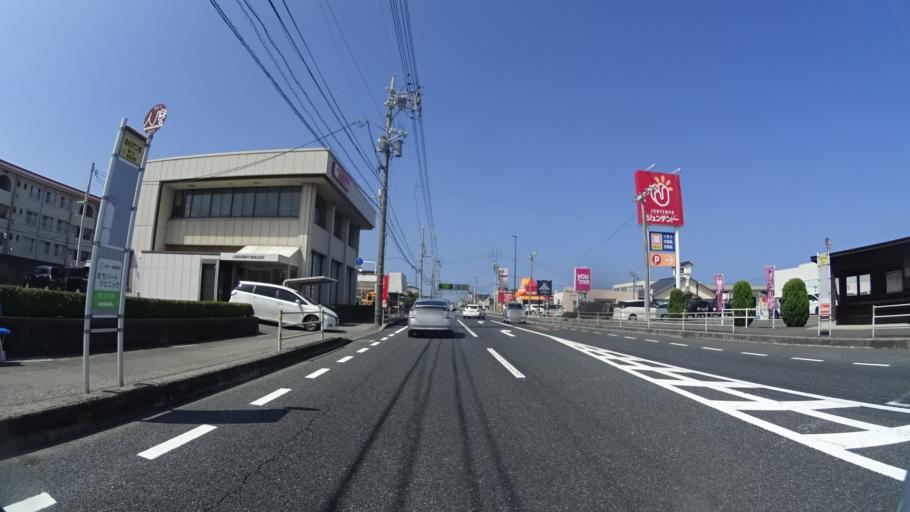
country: JP
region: Shimane
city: Masuda
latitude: 34.6897
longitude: 131.8164
